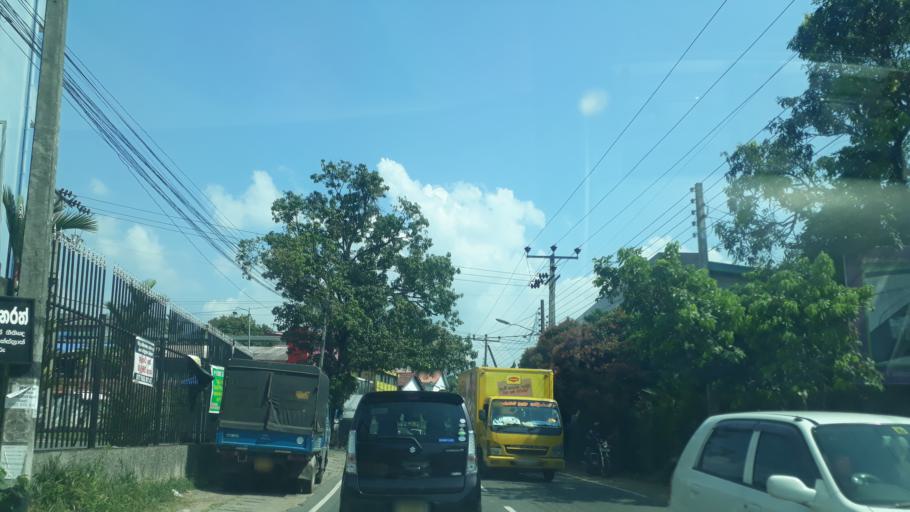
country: LK
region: Western
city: Gampaha
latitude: 7.0885
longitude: 80.0059
